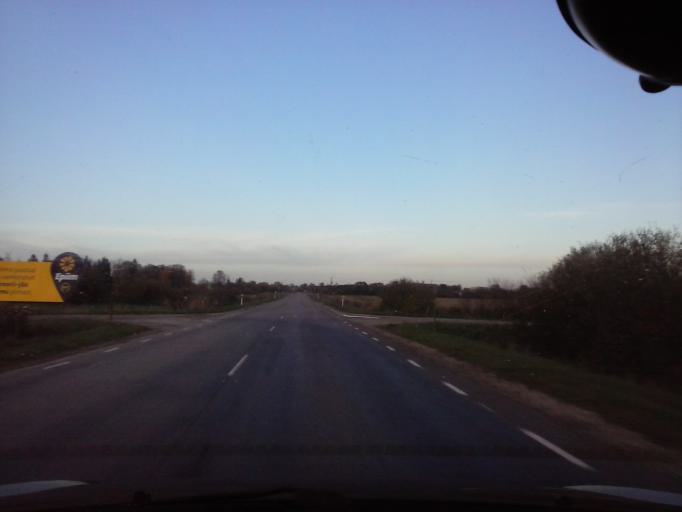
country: EE
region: Harju
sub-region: Nissi vald
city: Turba
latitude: 58.9107
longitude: 24.1457
